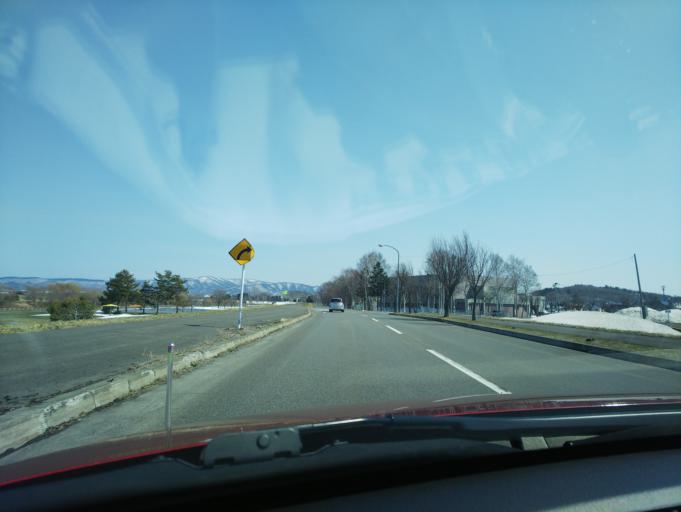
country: JP
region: Hokkaido
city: Nayoro
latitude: 44.1906
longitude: 142.3940
